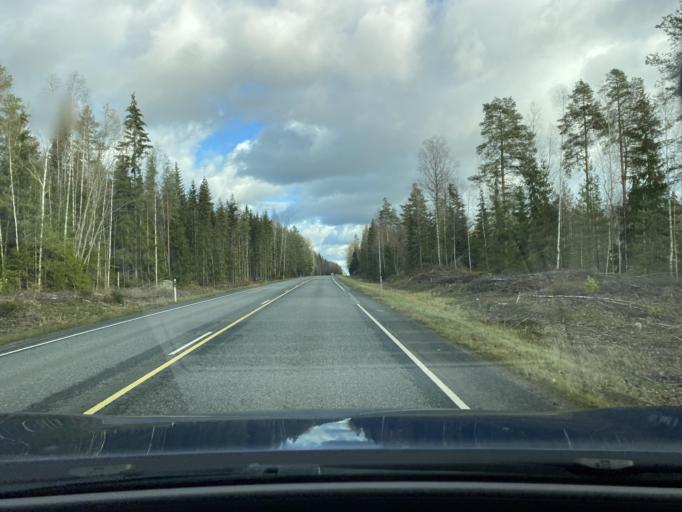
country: FI
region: Haeme
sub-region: Forssa
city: Humppila
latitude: 60.9352
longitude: 23.2583
